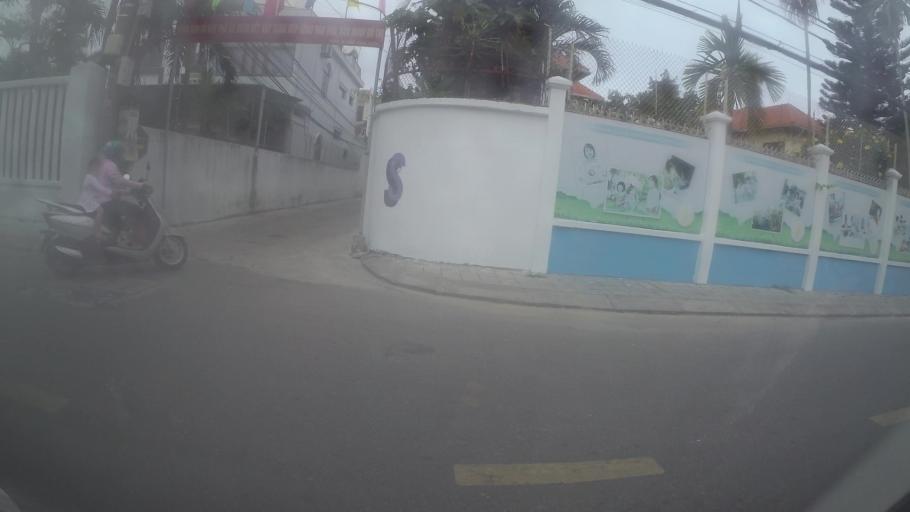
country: VN
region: Da Nang
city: Son Tra
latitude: 16.0431
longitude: 108.2453
